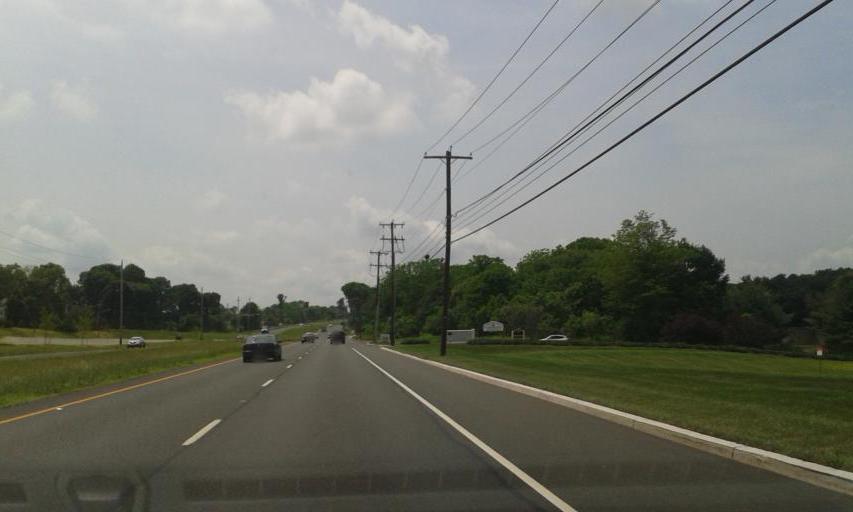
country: US
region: New Jersey
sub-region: Hunterdon County
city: Lebanon
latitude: 40.6440
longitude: -74.8413
